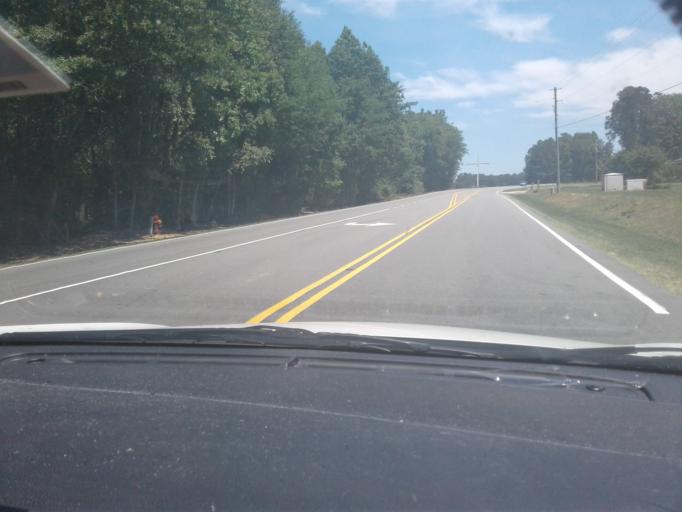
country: US
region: North Carolina
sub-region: Harnett County
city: Lillington
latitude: 35.4726
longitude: -78.8269
